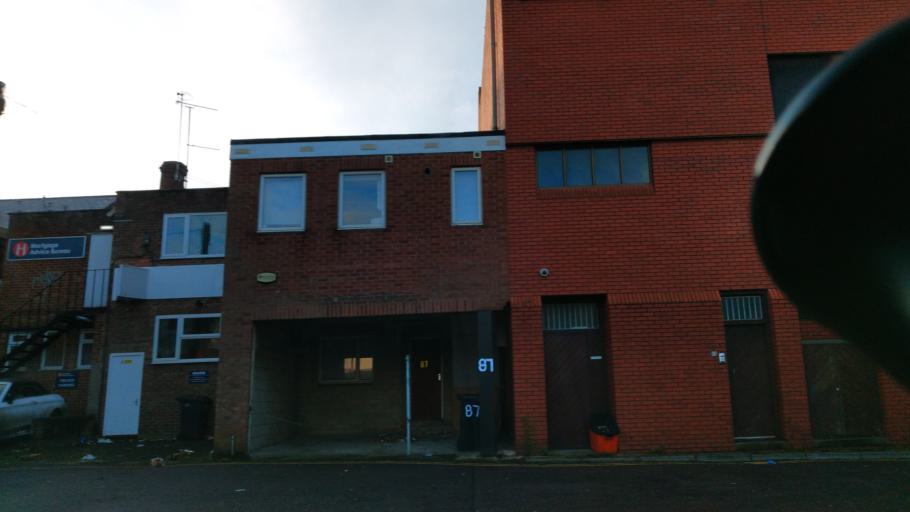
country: GB
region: England
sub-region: Borough of Swindon
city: Swindon
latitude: 51.5595
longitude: -1.7861
